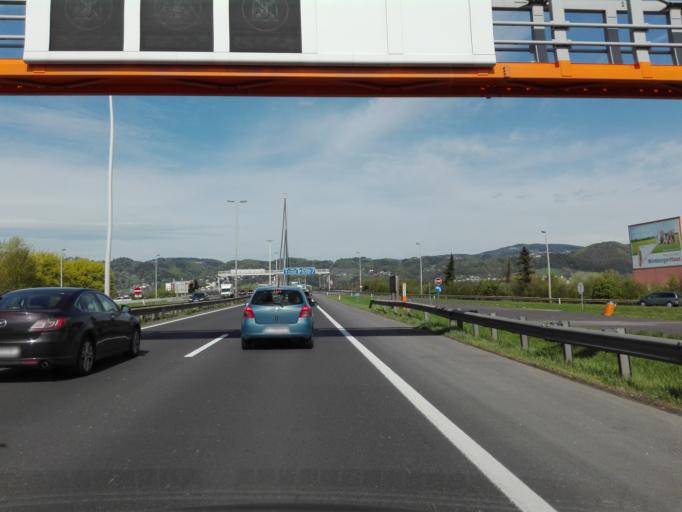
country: AT
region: Upper Austria
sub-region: Linz Stadt
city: Linz
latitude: 48.3177
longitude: 14.3024
